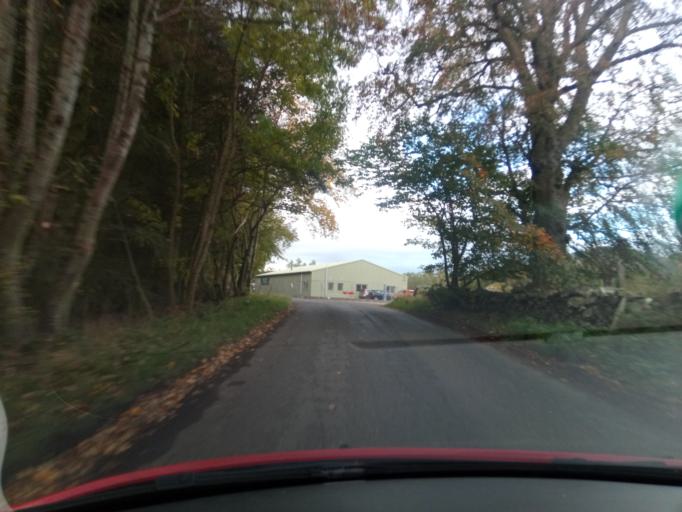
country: GB
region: Scotland
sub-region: The Scottish Borders
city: Peebles
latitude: 55.6446
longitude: -3.1660
